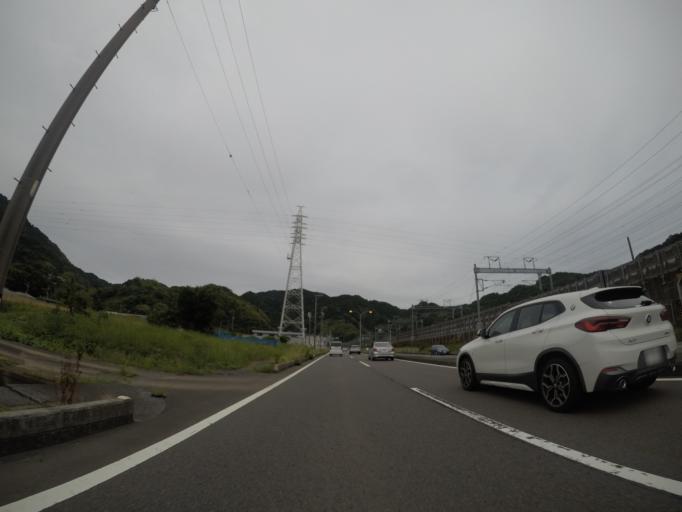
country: JP
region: Shizuoka
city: Yaizu
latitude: 34.8902
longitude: 138.3286
